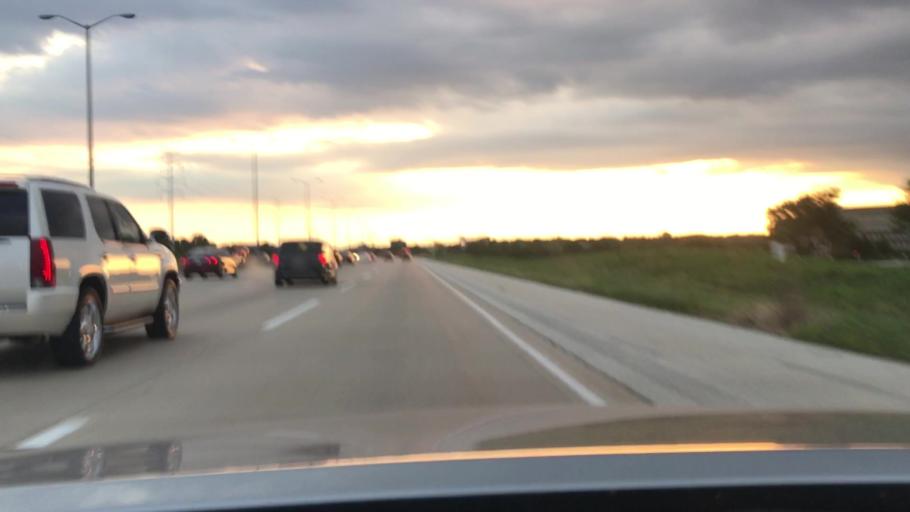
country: US
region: Illinois
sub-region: DuPage County
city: Warrenville
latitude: 41.8066
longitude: -88.1637
